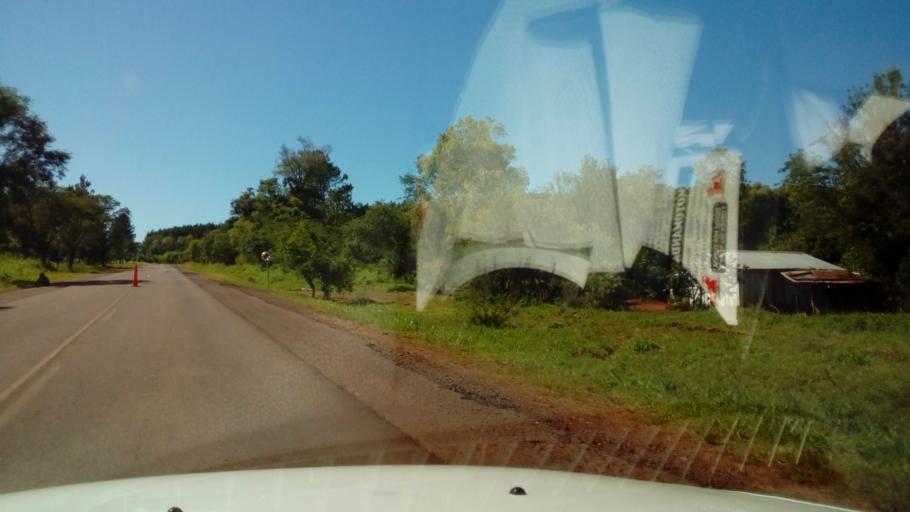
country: AR
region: Misiones
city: Almafuerte
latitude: -27.5555
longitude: -55.4206
